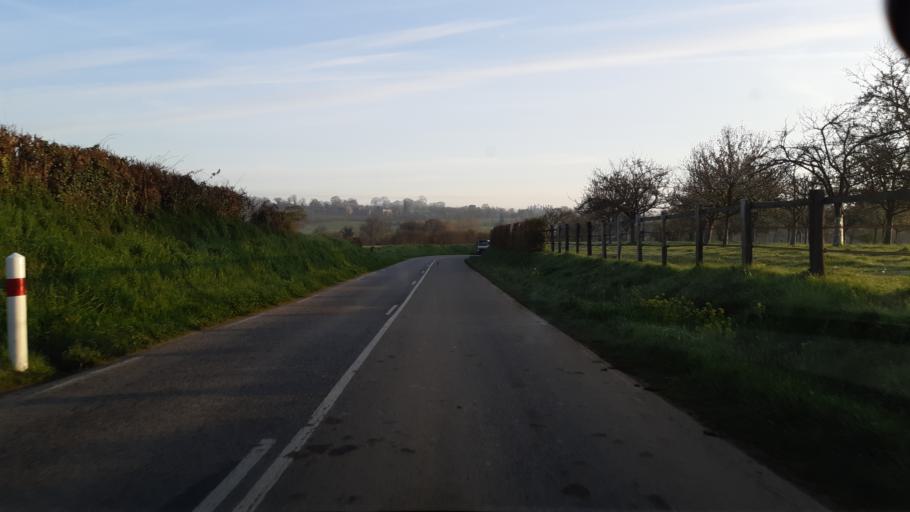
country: FR
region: Lower Normandy
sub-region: Departement de la Manche
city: Agneaux
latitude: 49.0646
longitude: -1.1325
